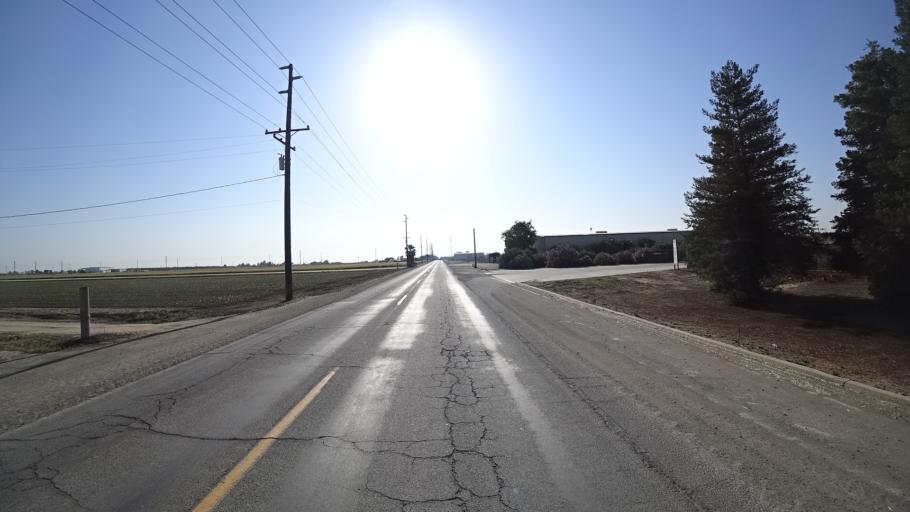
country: US
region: California
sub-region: Kings County
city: Home Garden
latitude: 36.3135
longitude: -119.5978
